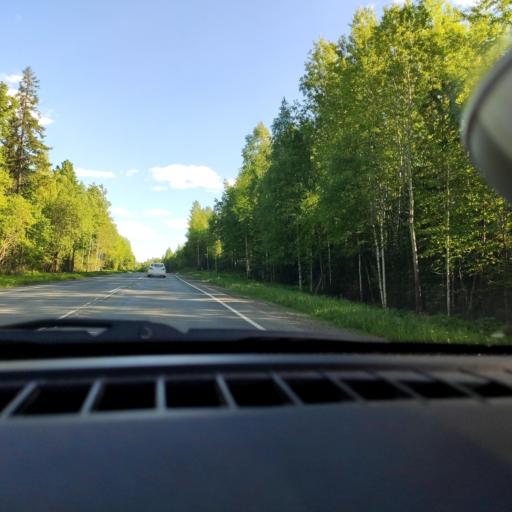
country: RU
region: Perm
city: Perm
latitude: 58.2280
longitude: 56.1633
